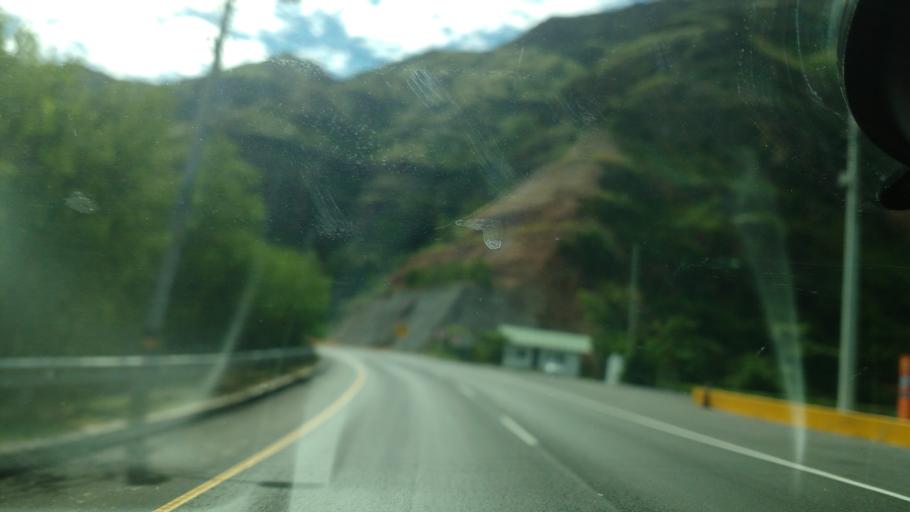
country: CO
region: Tolima
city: Valle de San Juan
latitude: 4.2855
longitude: -75.0222
